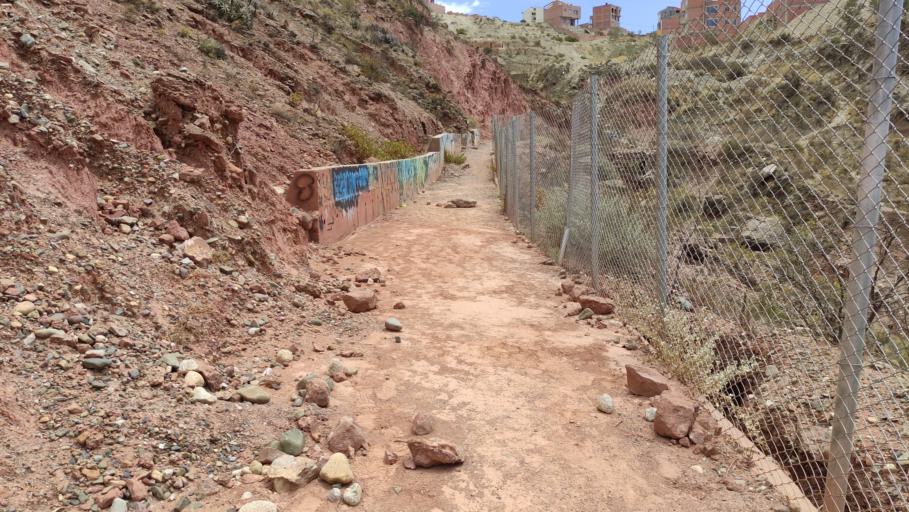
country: BO
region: La Paz
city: La Paz
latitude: -16.5525
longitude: -68.0946
